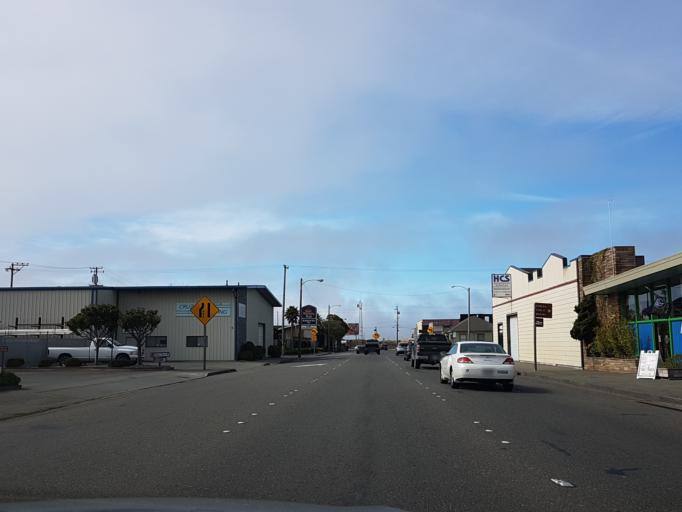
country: US
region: California
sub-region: Humboldt County
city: Eureka
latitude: 40.8019
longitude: -124.1726
